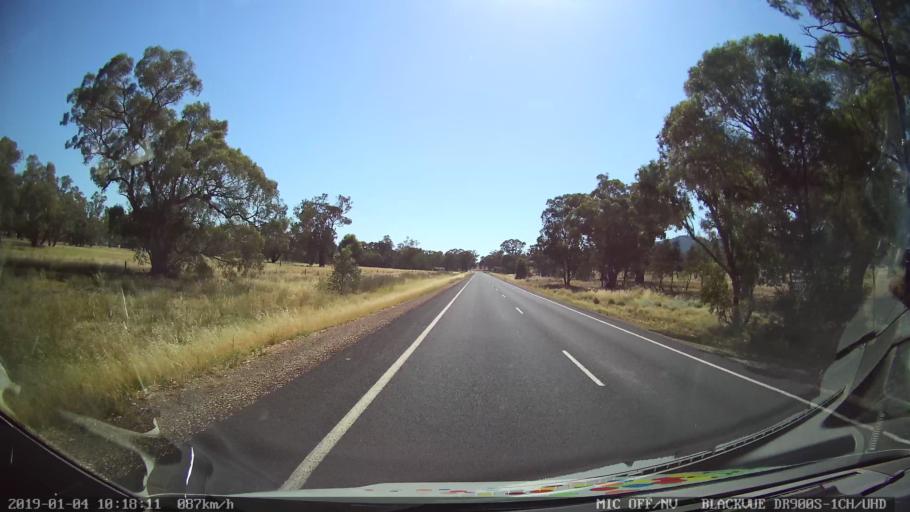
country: AU
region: New South Wales
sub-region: Cabonne
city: Canowindra
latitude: -33.3828
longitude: 148.4627
